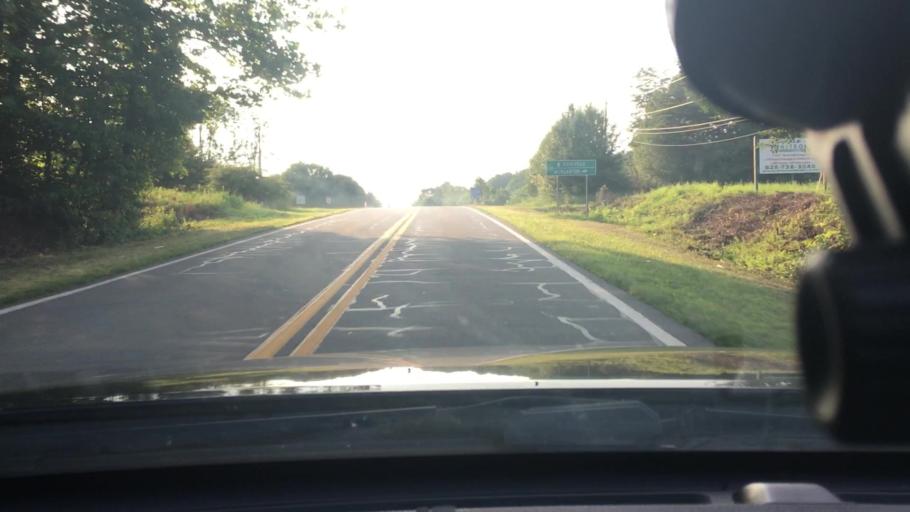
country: US
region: North Carolina
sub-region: McDowell County
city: West Marion
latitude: 35.6321
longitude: -81.9996
